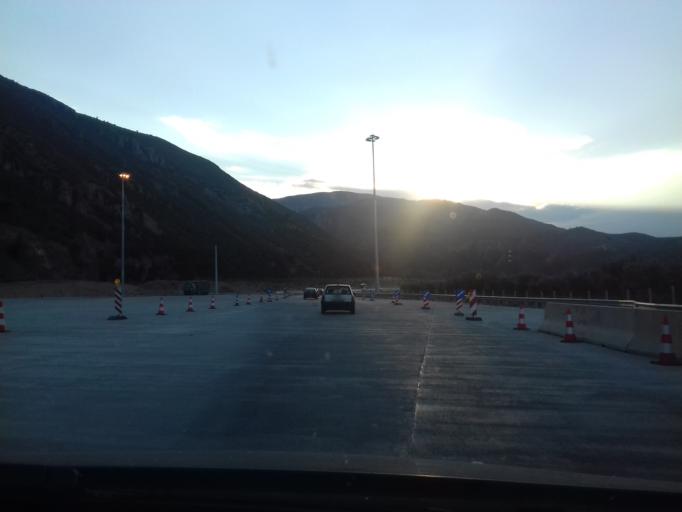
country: GR
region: West Greece
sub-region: Nomos Achaias
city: Temeni
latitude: 38.1912
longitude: 22.1649
